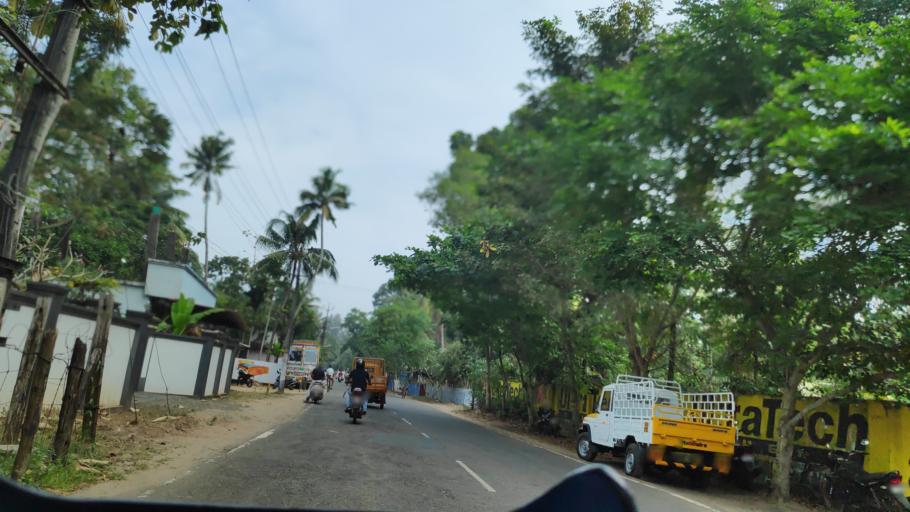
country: IN
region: Kerala
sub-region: Alappuzha
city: Vayalar
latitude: 9.7157
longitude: 76.3593
